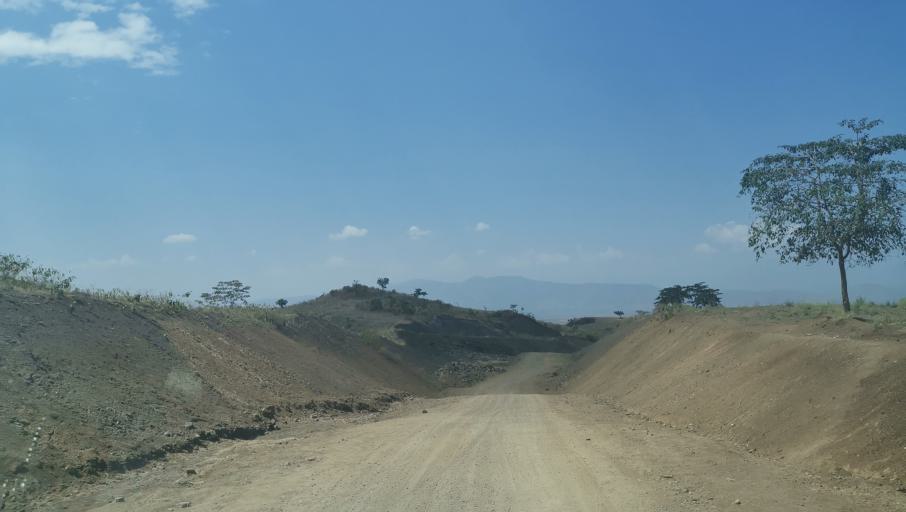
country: ET
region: Southern Nations, Nationalities, and People's Region
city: Arba Minch'
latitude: 6.3316
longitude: 37.3363
